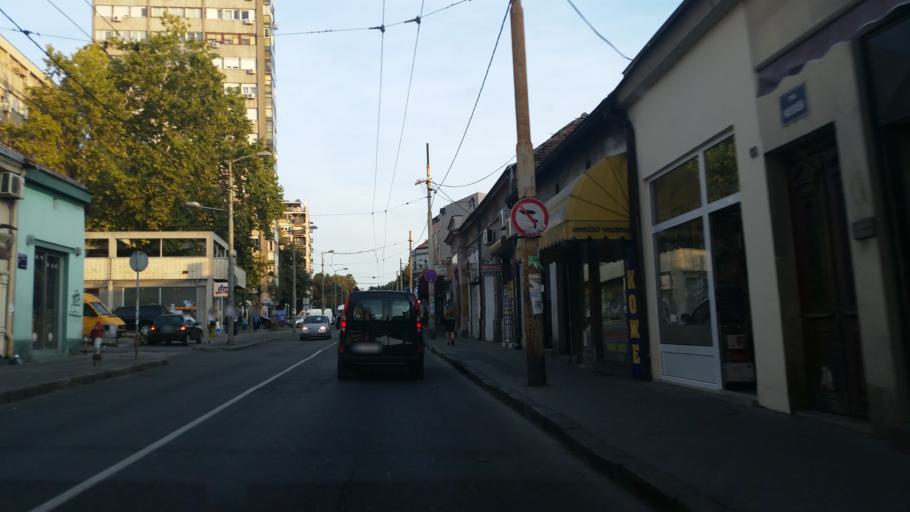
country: RS
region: Central Serbia
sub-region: Belgrade
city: Vracar
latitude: 44.7993
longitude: 20.4721
